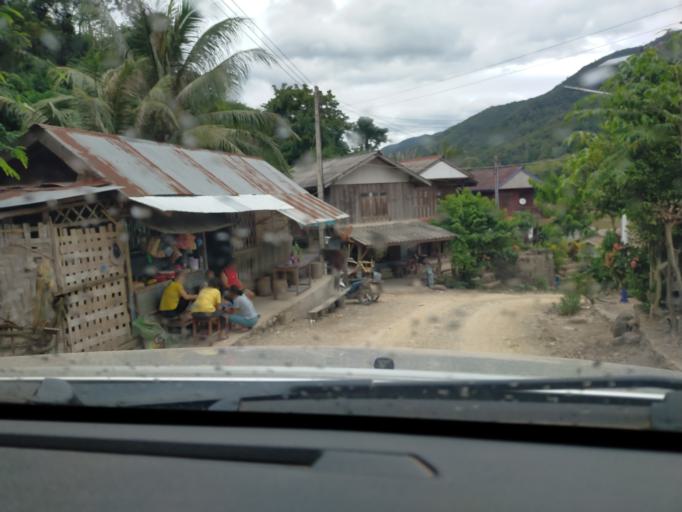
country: TH
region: Nan
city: Chaloem Phra Kiat
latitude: 19.8175
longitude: 101.3580
